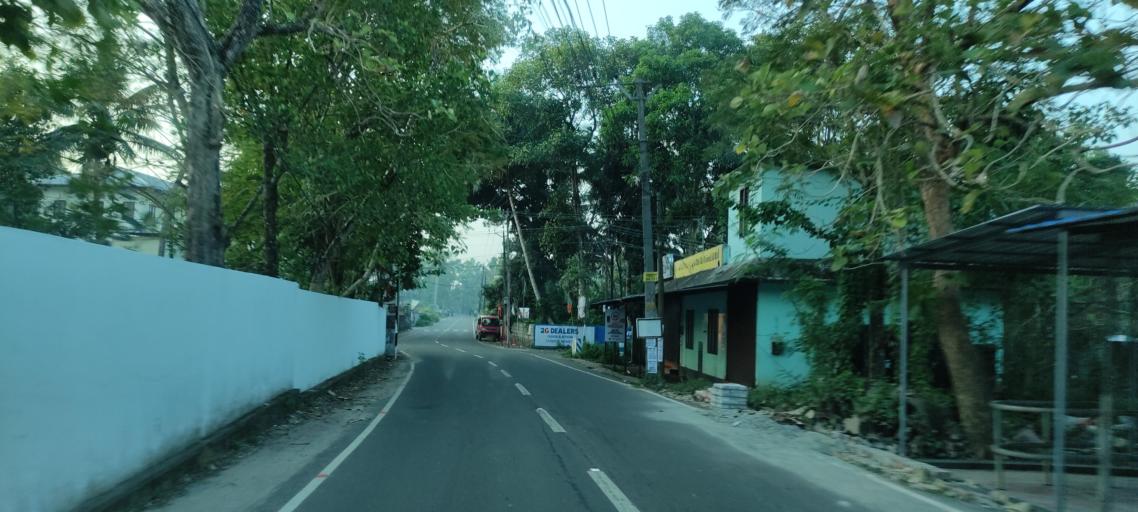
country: IN
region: Kerala
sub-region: Alappuzha
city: Alleppey
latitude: 9.4537
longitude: 76.3449
